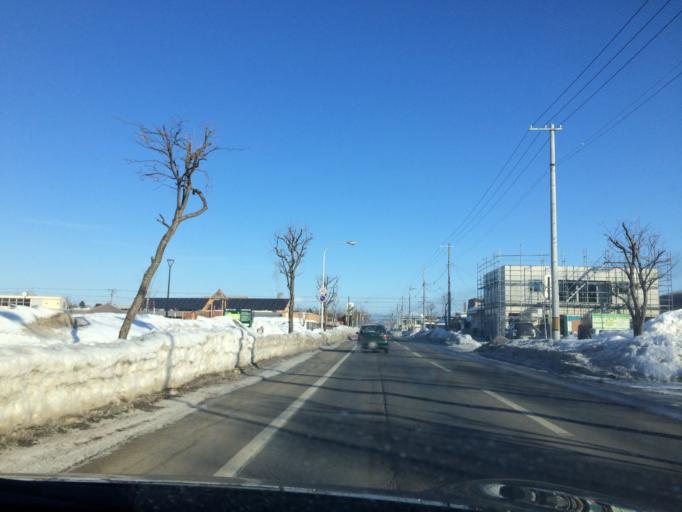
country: JP
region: Hokkaido
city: Obihiro
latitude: 42.9144
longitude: 143.0539
